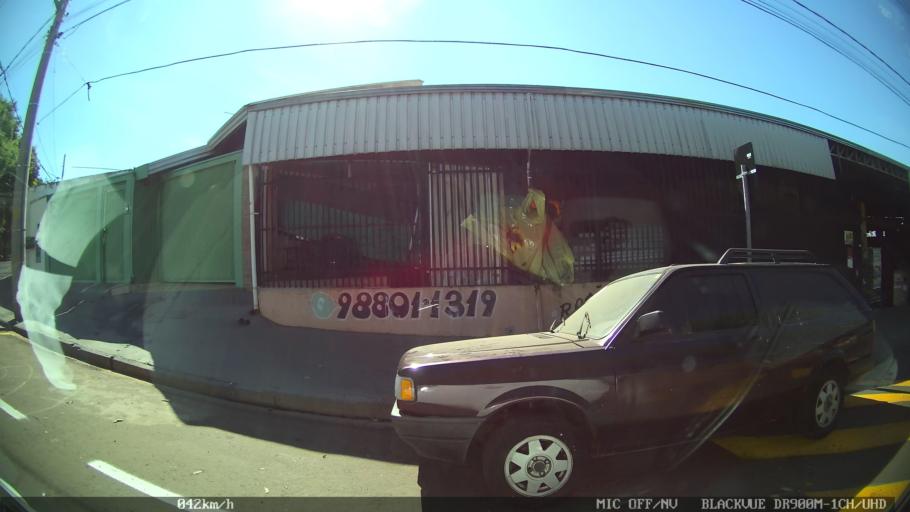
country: BR
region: Sao Paulo
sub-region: Sao Jose Do Rio Preto
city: Sao Jose do Rio Preto
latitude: -20.7730
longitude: -49.4118
